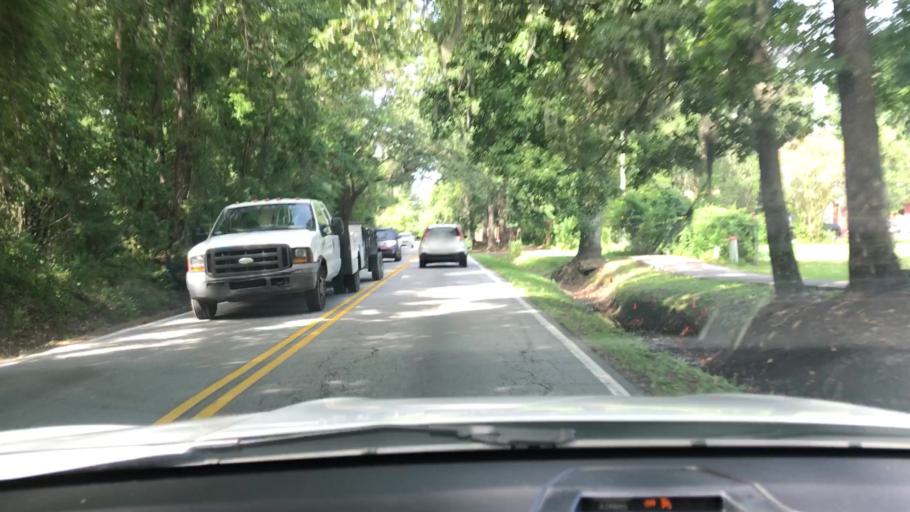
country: US
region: South Carolina
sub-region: Charleston County
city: Mount Pleasant
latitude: 32.8428
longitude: -79.8421
